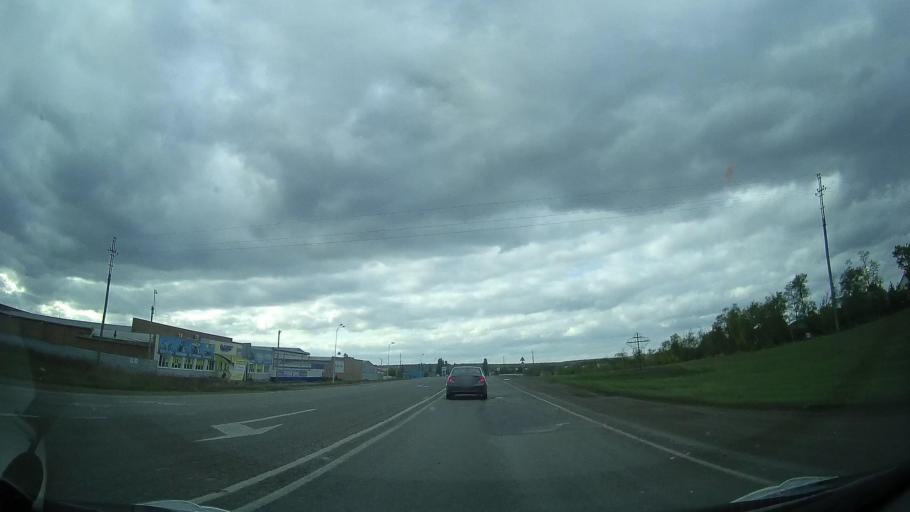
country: RU
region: Rostov
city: Kagal'nitskaya
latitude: 46.8748
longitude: 40.1609
